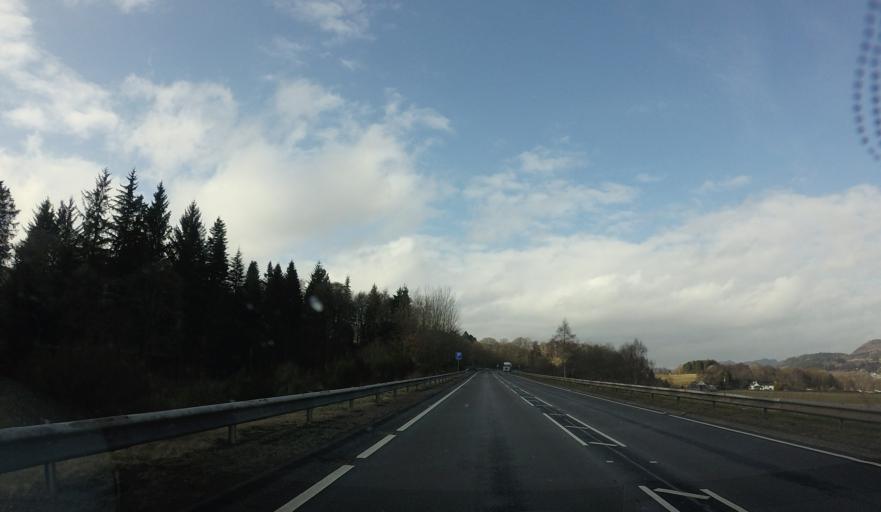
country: GB
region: Scotland
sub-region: Perth and Kinross
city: Pitlochry
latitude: 56.6909
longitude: -3.7213
